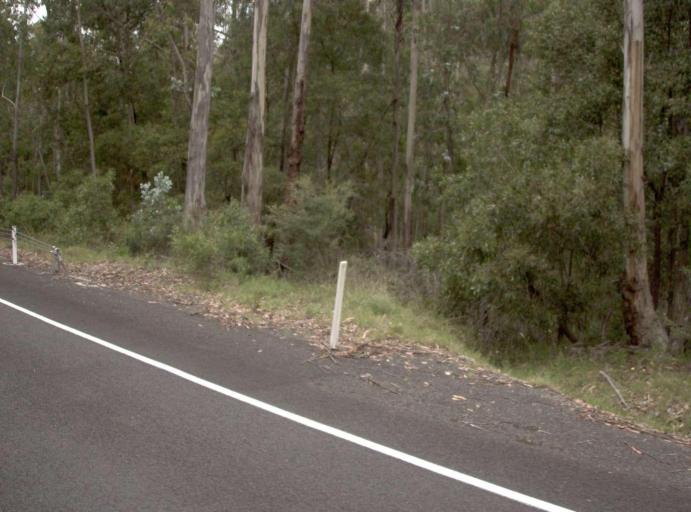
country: AU
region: New South Wales
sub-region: Bombala
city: Bombala
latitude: -37.2893
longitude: 149.2219
